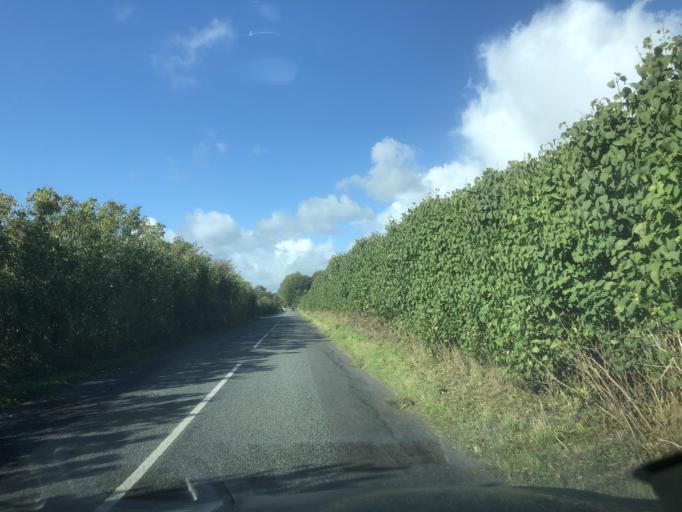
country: DK
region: South Denmark
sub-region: Faaborg-Midtfyn Kommune
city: Ringe
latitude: 55.2444
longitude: 10.3773
